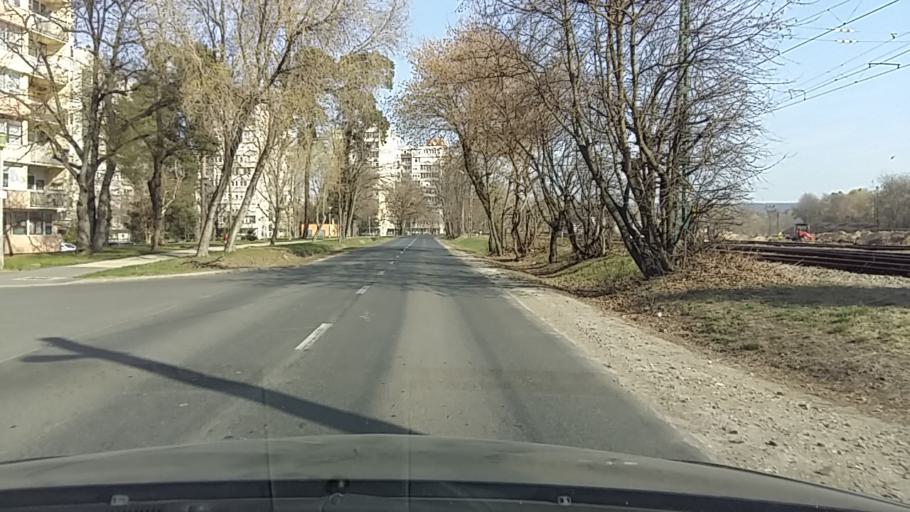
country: HU
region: Pest
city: Godollo
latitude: 47.5945
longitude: 19.3572
